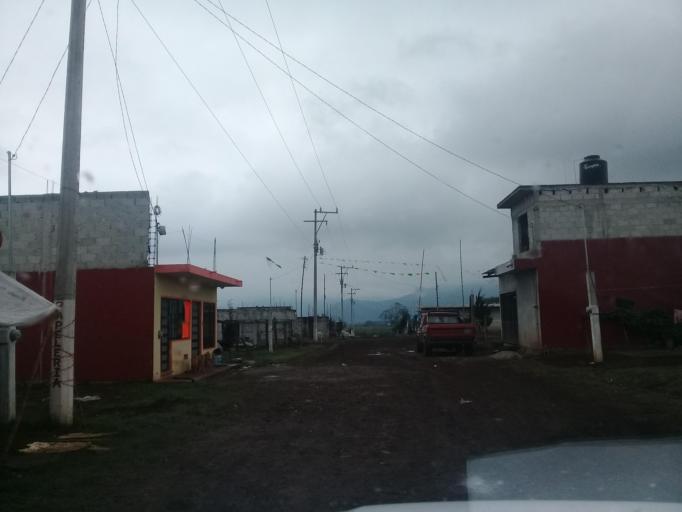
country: MX
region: Veracruz
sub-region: Cordoba
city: San Jose de Tapia
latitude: 18.8529
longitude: -96.9581
